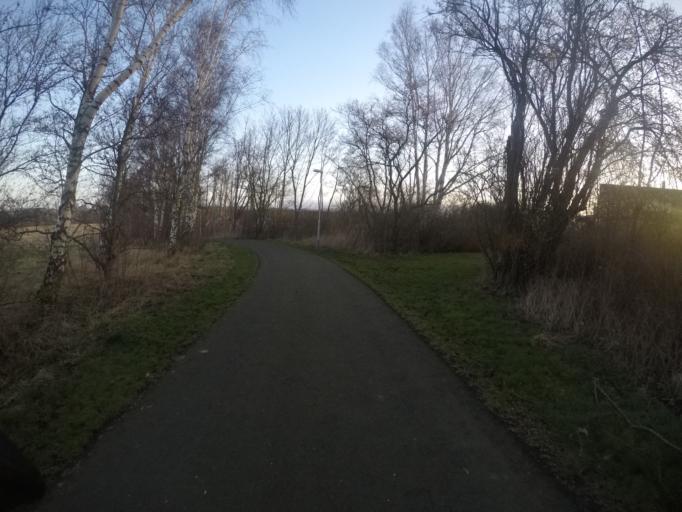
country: SE
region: Halland
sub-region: Laholms Kommun
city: Laholm
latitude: 56.5072
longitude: 13.0198
